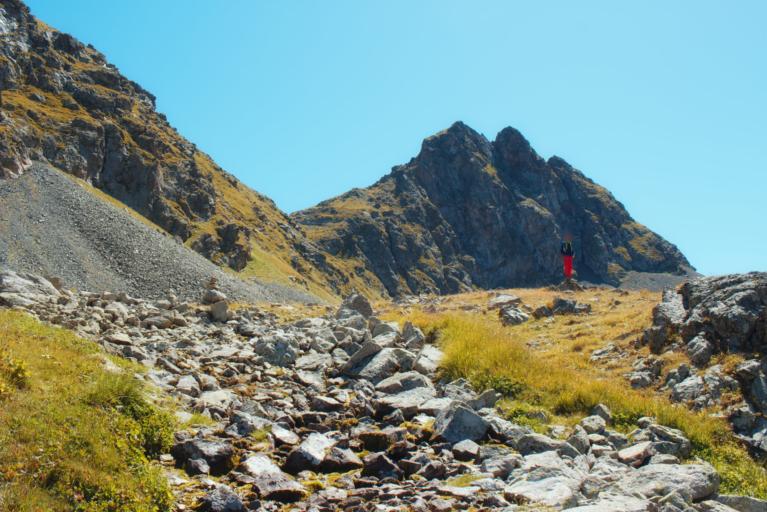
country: RU
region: Karachayevo-Cherkesiya
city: Nizhniy Arkhyz
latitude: 43.6030
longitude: 41.1674
